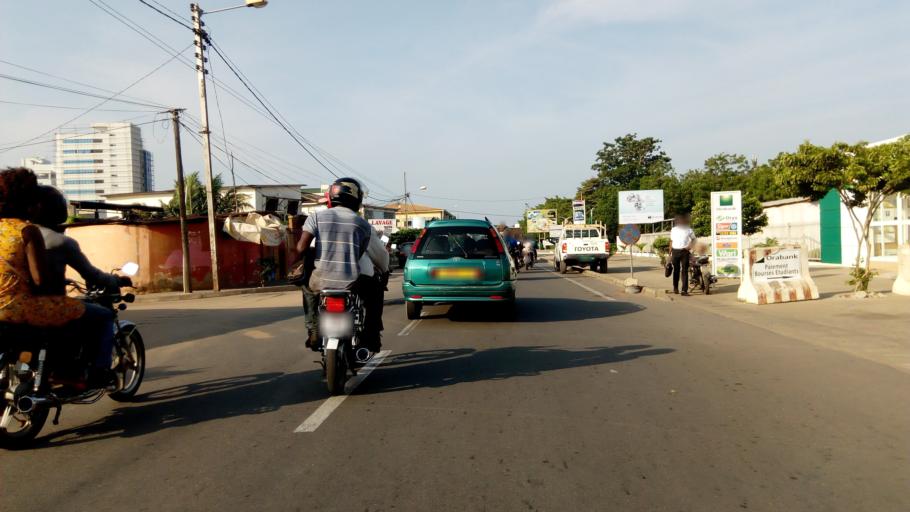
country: TG
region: Maritime
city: Lome
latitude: 6.1307
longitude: 1.2138
